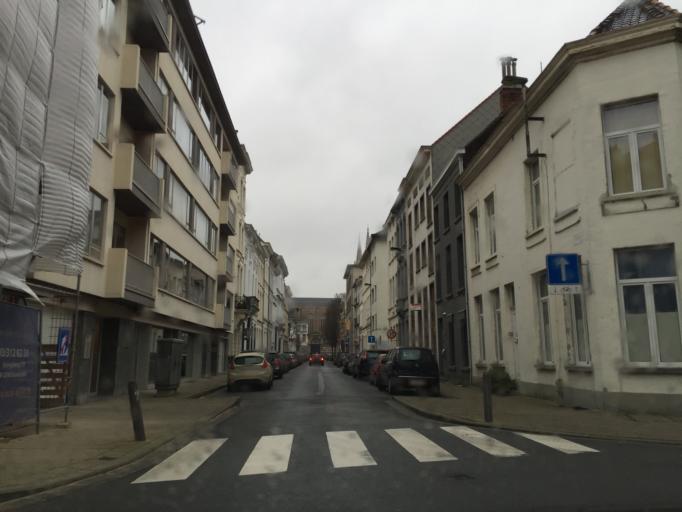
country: BE
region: Flanders
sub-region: Provincie Antwerpen
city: Antwerpen
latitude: 51.2106
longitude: 4.4052
